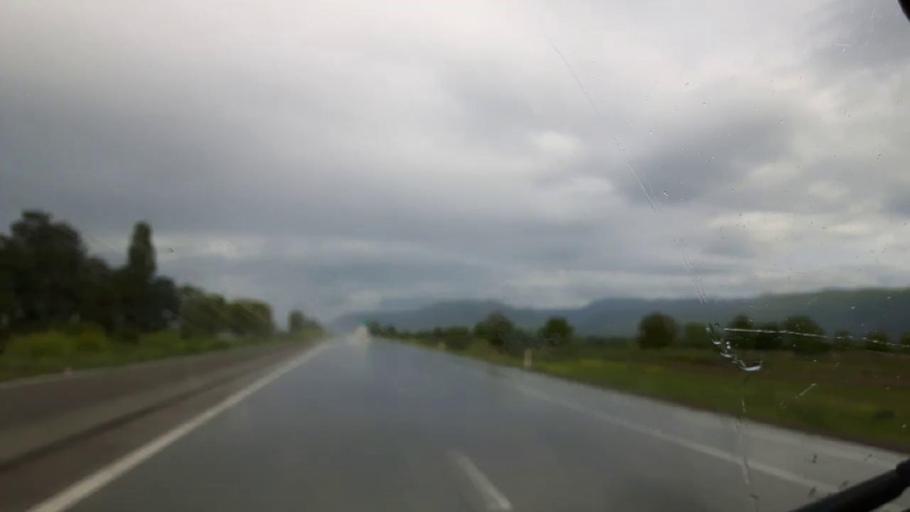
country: GE
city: Agara
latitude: 42.0395
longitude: 43.9322
